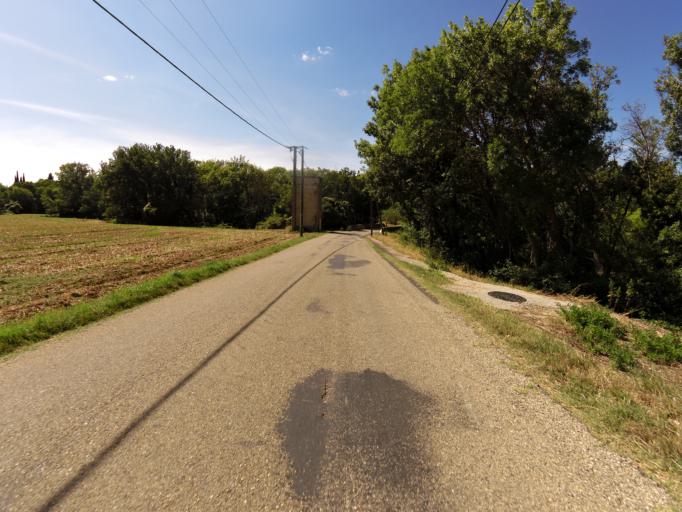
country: FR
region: Languedoc-Roussillon
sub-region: Departement du Gard
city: Quissac
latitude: 43.9177
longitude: 4.0480
